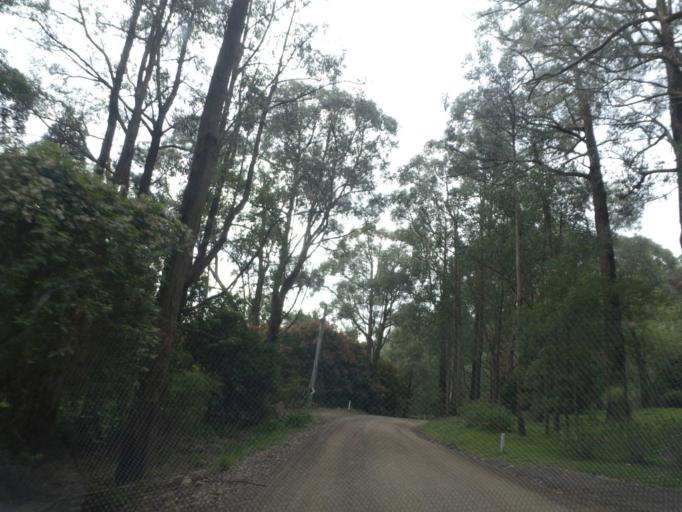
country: AU
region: Victoria
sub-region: Yarra Ranges
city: Olinda
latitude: -37.8591
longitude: 145.3447
